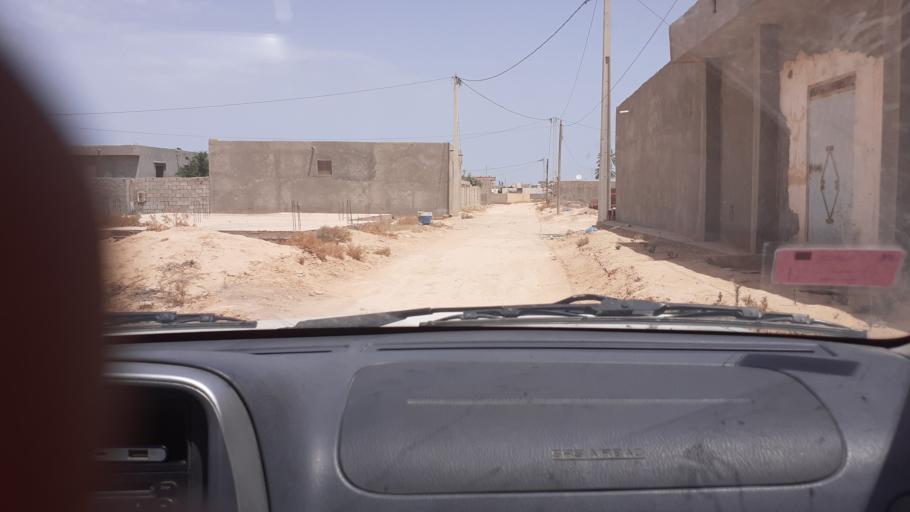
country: TN
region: Qabis
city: Matmata
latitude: 33.6089
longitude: 10.2894
